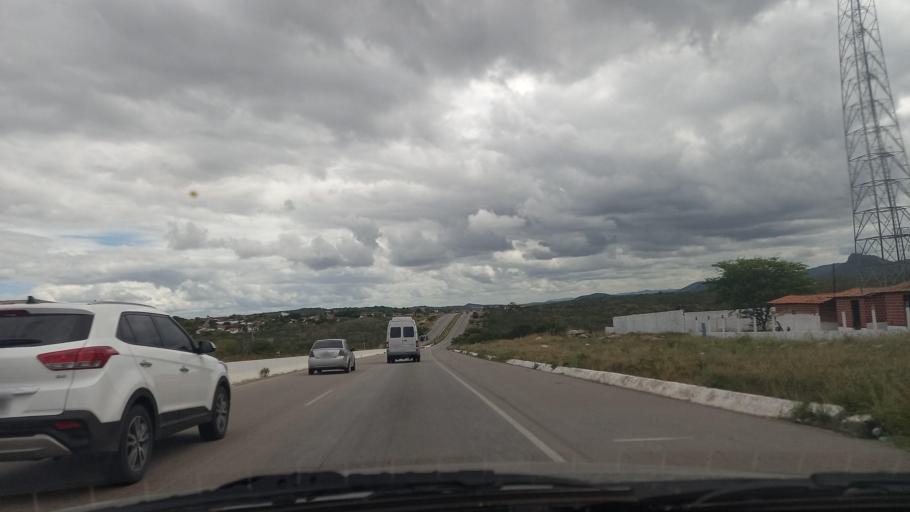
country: BR
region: Pernambuco
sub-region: Caruaru
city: Caruaru
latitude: -8.3183
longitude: -36.0590
